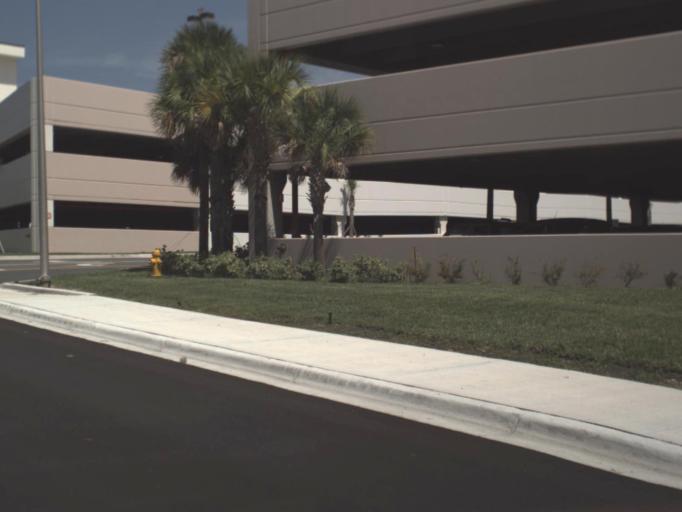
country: US
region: Florida
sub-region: Alachua County
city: Gainesville
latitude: 29.6347
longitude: -82.3483
